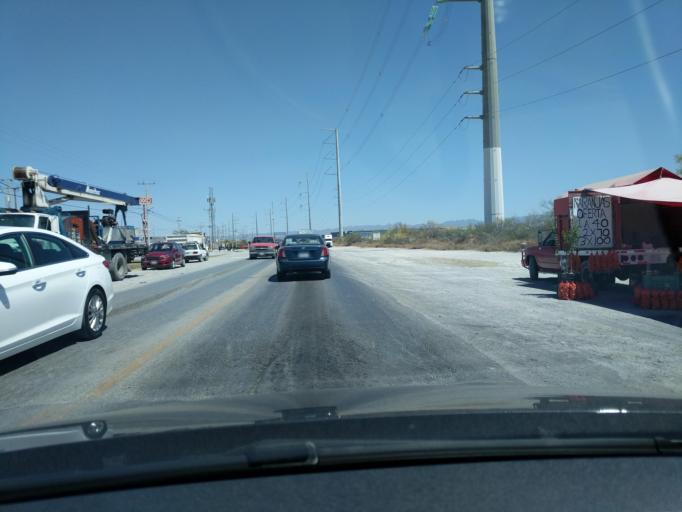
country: MX
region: Nuevo Leon
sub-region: Apodaca
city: Artemio Trevino
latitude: 25.8332
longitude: -100.1404
